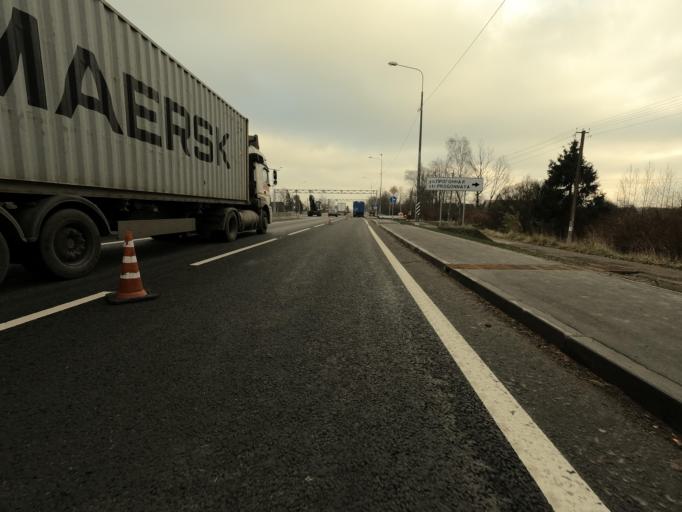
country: RU
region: Leningrad
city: Mga
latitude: 59.7217
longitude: 31.0997
